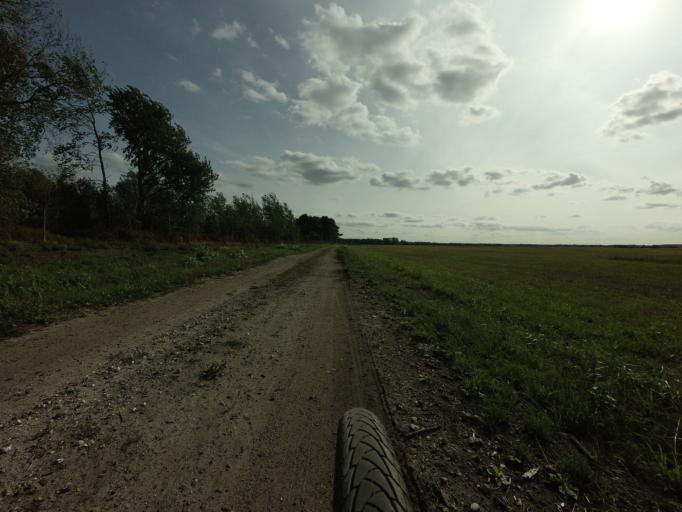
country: DK
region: Zealand
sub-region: Vordingborg Kommune
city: Praesto
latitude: 55.1484
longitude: 12.0923
